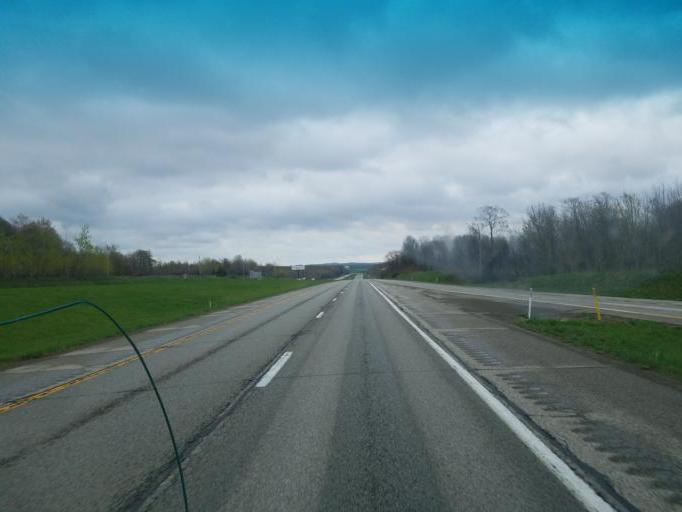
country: US
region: Pennsylvania
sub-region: Erie County
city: North East
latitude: 42.1361
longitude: -79.8193
